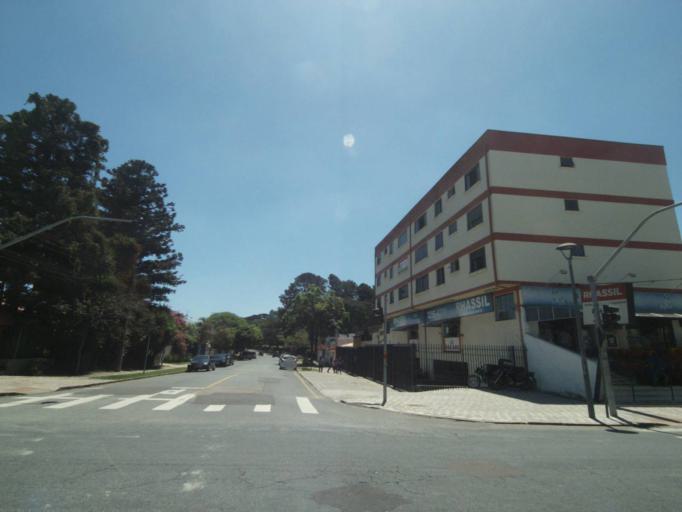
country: BR
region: Parana
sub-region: Curitiba
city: Curitiba
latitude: -25.3927
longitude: -49.2266
